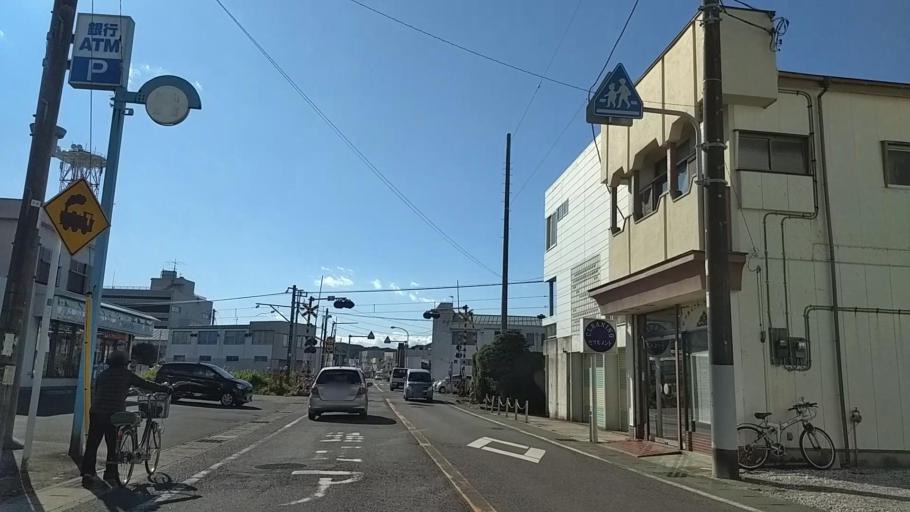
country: JP
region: Chiba
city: Tateyama
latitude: 34.9910
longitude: 139.8629
